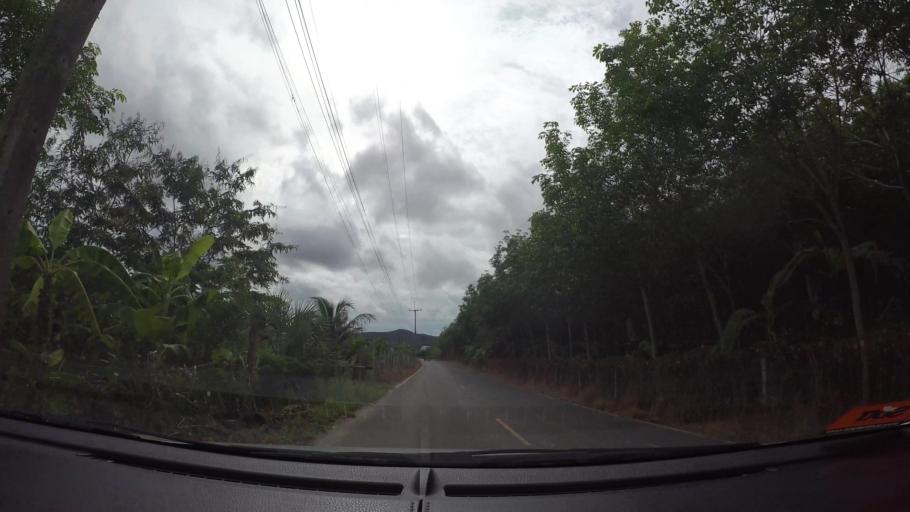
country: TH
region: Chon Buri
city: Sattahip
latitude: 12.7199
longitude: 100.9087
